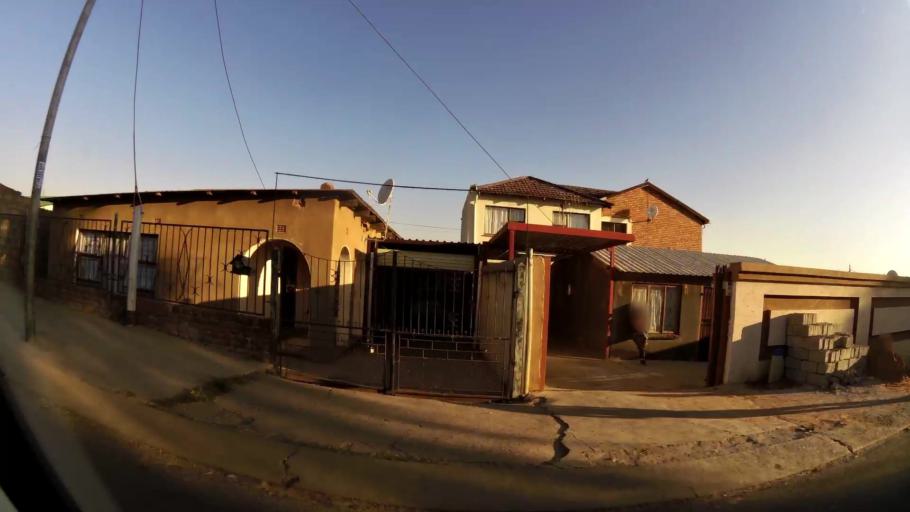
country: ZA
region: Gauteng
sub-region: City of Tshwane Metropolitan Municipality
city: Cullinan
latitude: -25.7243
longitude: 28.3867
